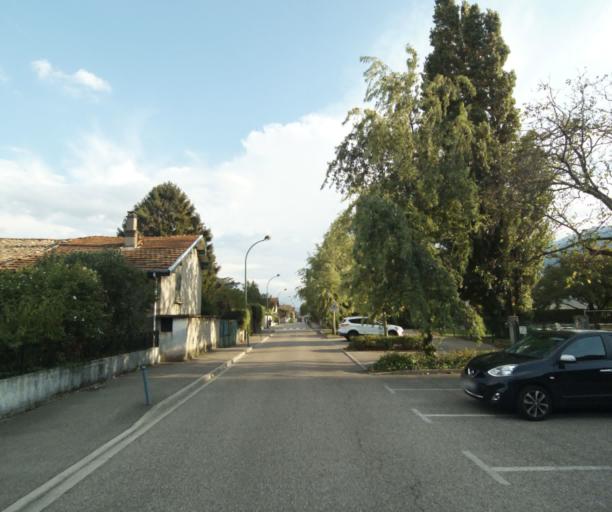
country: FR
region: Rhone-Alpes
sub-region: Departement de l'Isere
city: Seyssinet-Pariset
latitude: 45.1698
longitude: 5.6968
